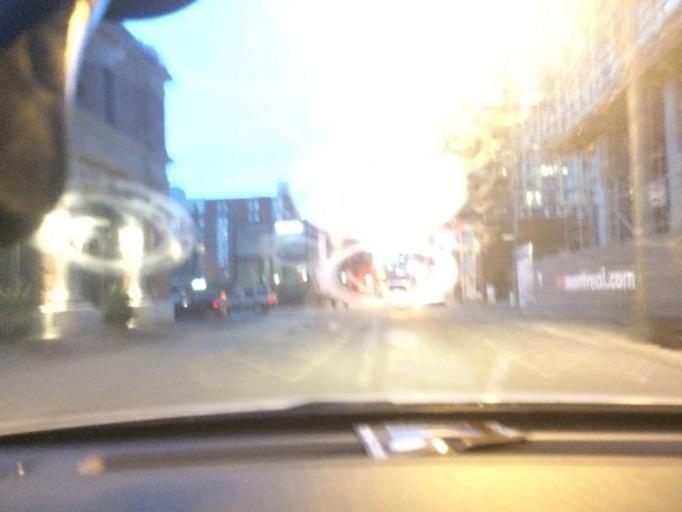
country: CA
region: Quebec
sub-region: Montreal
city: Montreal
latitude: 45.4932
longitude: -73.5600
